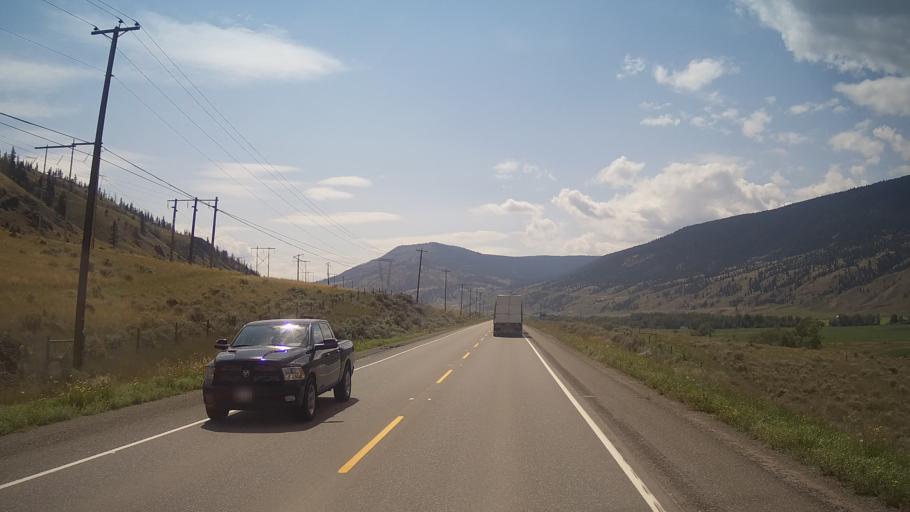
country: CA
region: British Columbia
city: Cache Creek
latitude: 50.8709
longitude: -121.3908
